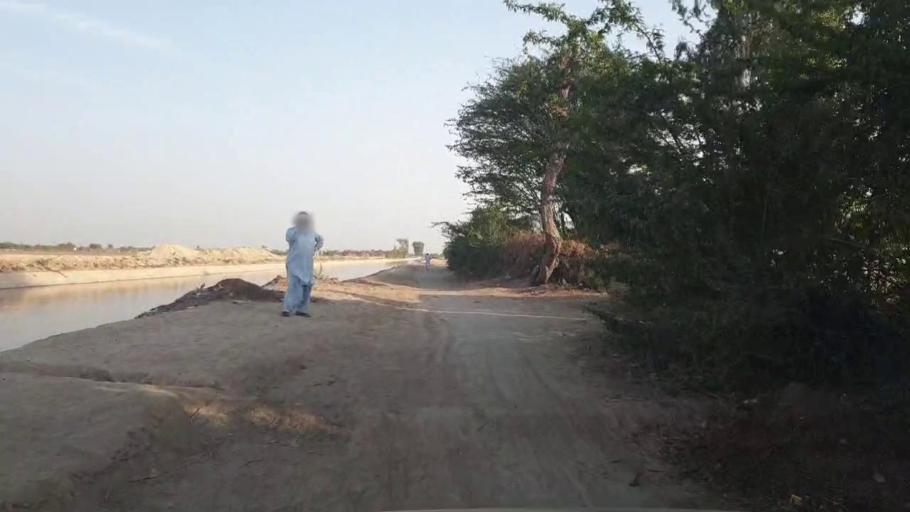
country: PK
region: Sindh
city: Dhoro Naro
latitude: 25.4942
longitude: 69.5632
